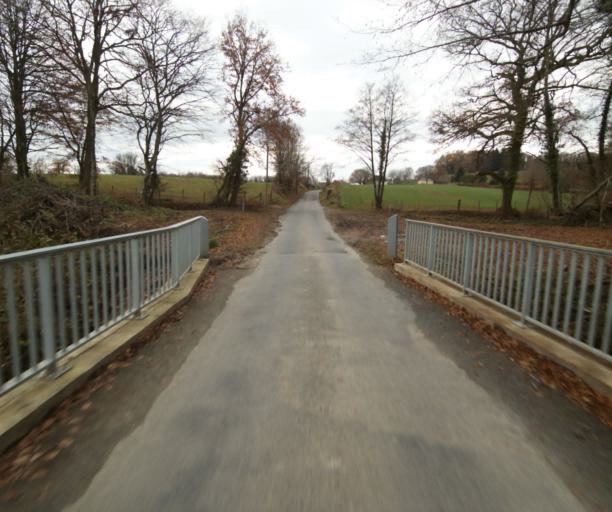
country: FR
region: Limousin
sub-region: Departement de la Correze
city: Chameyrat
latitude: 45.2409
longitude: 1.7087
